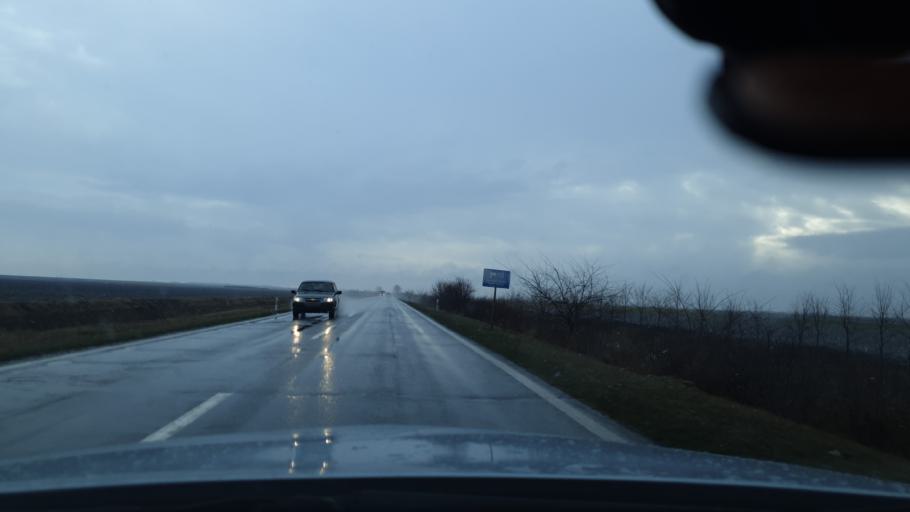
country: RS
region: Autonomna Pokrajina Vojvodina
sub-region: Juznobanatski Okrug
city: Pancevo
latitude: 44.8433
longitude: 20.7921
